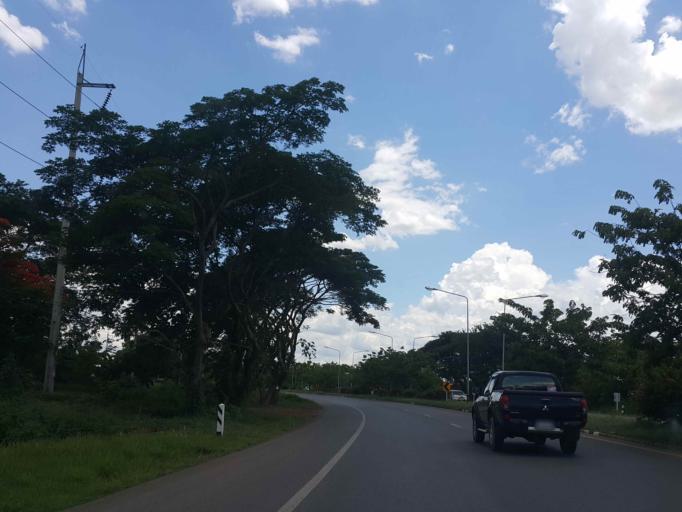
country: TH
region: Phrae
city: Nong Muang Khai
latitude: 18.2234
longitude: 100.1998
